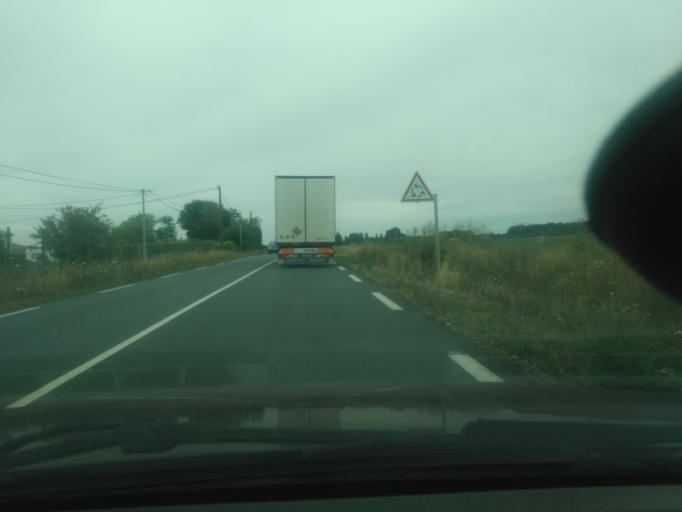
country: FR
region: Poitou-Charentes
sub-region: Departement de la Vienne
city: Sevres-Anxaumont
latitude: 46.5588
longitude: 0.4828
